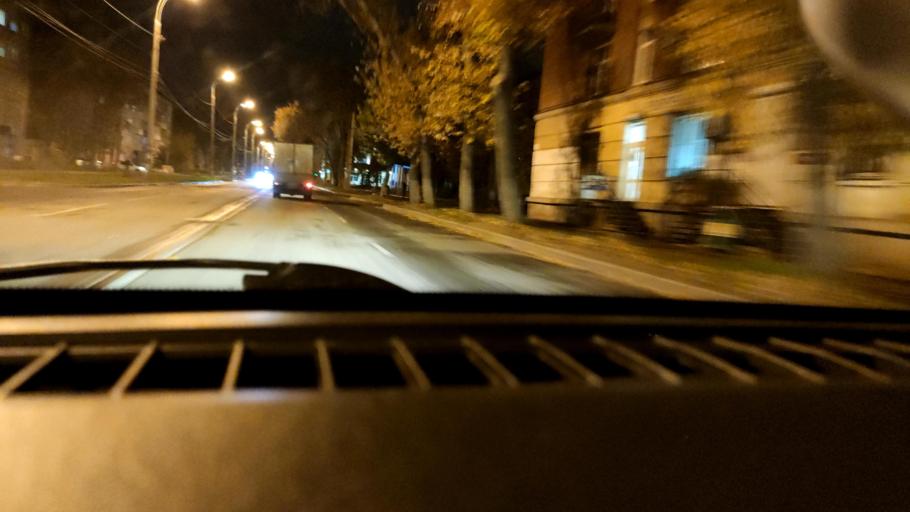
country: RU
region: Samara
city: Samara
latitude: 53.2110
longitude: 50.2490
